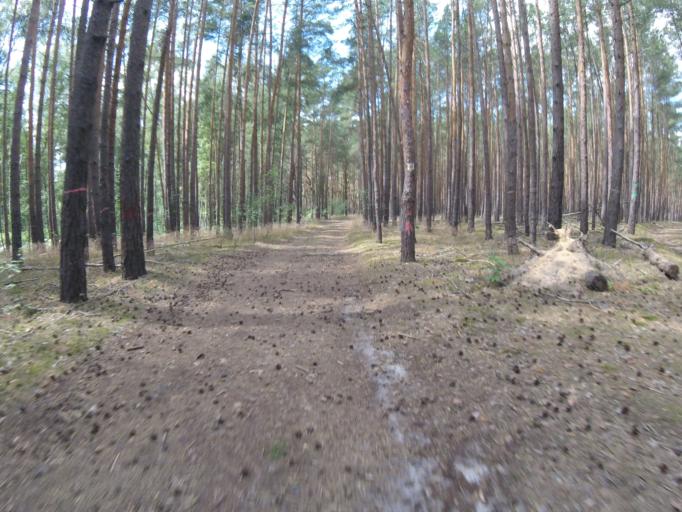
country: DE
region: Brandenburg
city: Gross Koris
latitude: 52.1999
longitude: 13.6456
